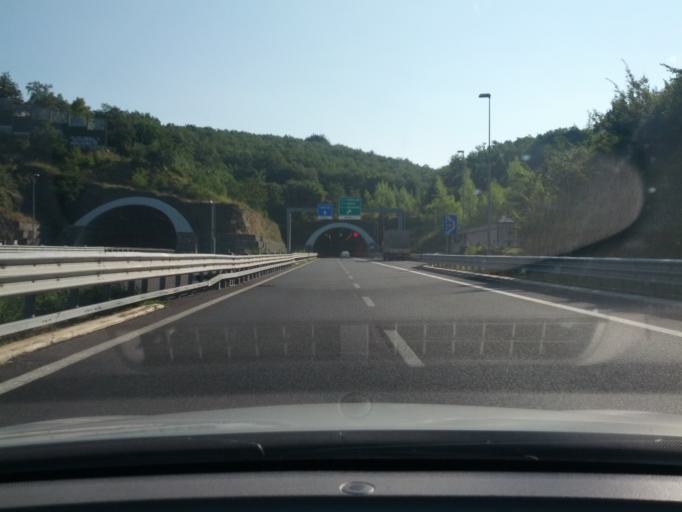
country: IT
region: Friuli Venezia Giulia
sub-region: Provincia di Trieste
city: Domio
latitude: 45.5975
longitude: 13.8082
